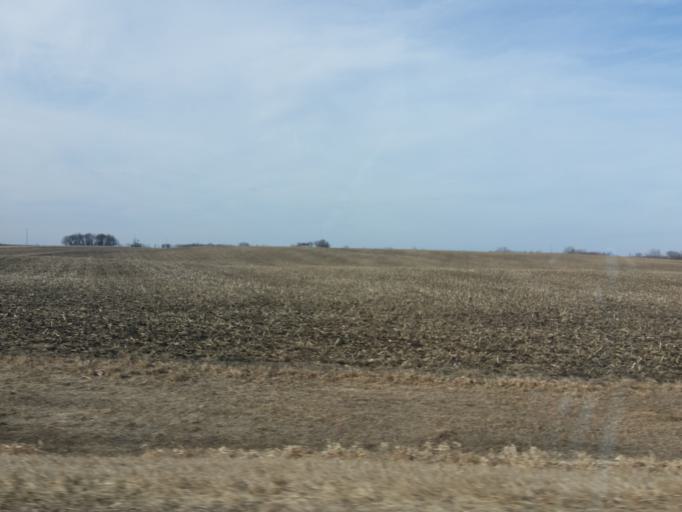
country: US
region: Minnesota
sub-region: Clay County
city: Barnesville
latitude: 46.4716
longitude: -96.3209
